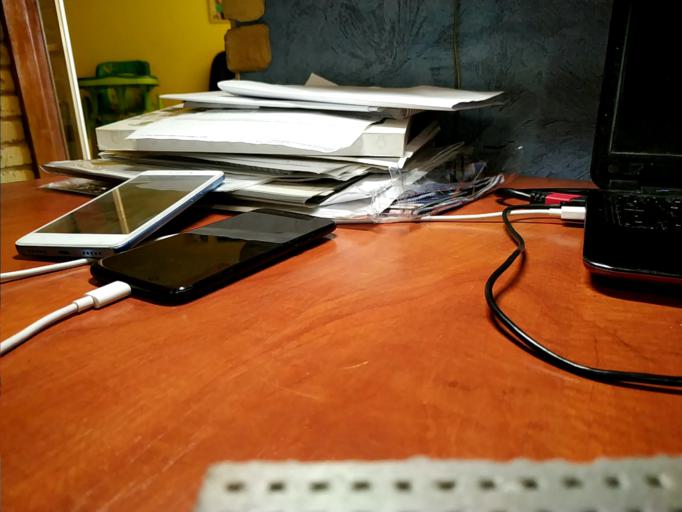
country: RU
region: Tverskaya
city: Kalashnikovo
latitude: 57.4079
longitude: 35.1851
